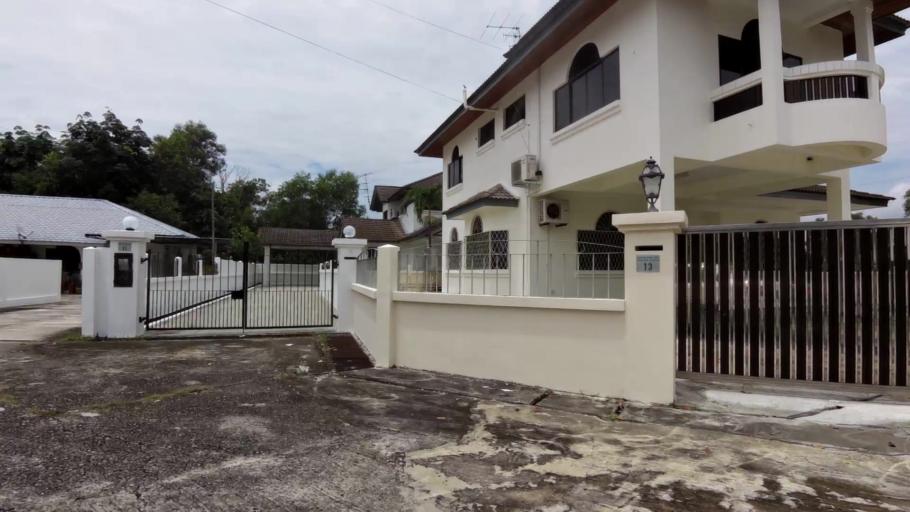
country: BN
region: Brunei and Muara
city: Bandar Seri Begawan
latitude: 4.8930
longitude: 114.9236
